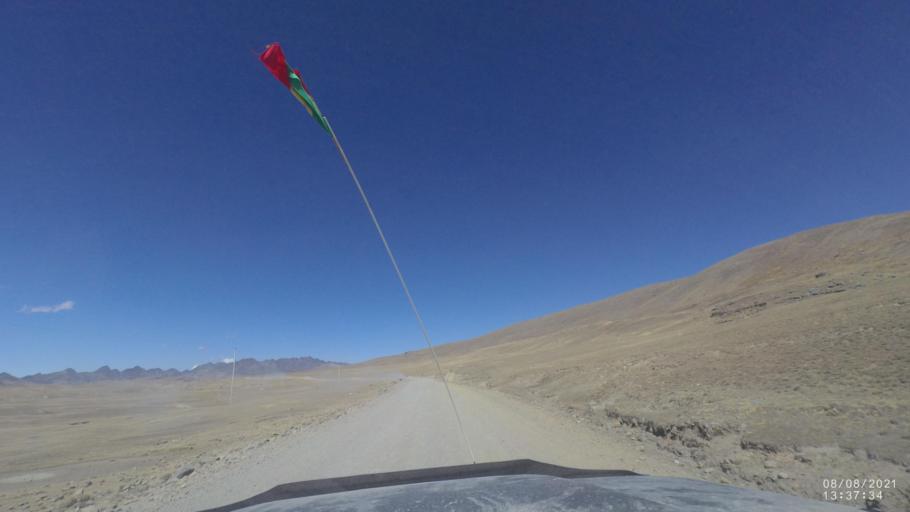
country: BO
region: Cochabamba
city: Colchani
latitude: -17.0808
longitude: -66.4958
